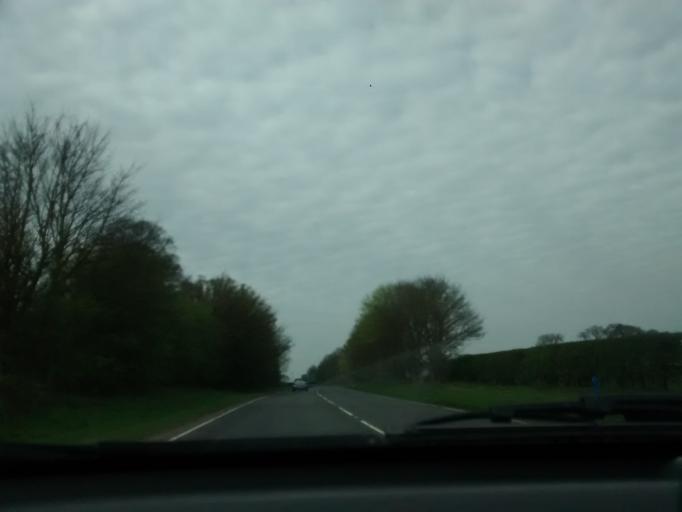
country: GB
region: England
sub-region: Oxfordshire
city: Bicester
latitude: 51.9631
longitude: -1.0982
